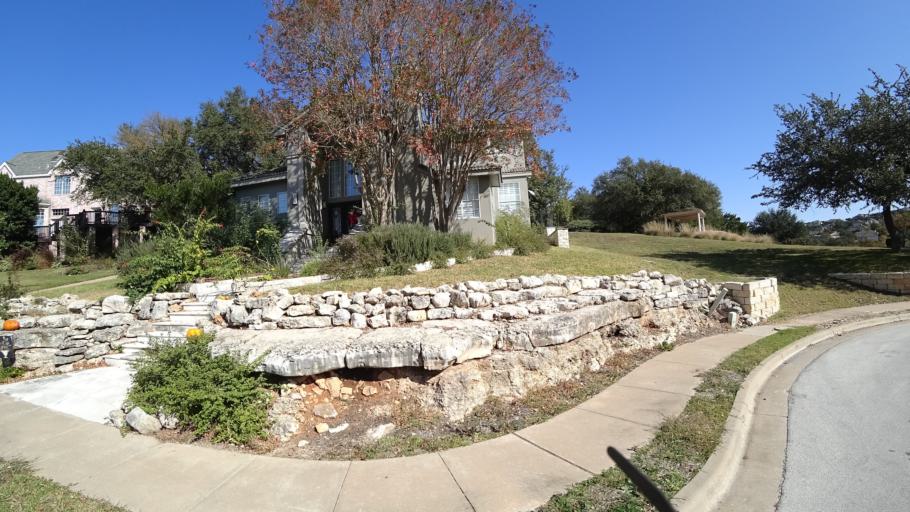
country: US
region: Texas
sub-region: Travis County
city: Lost Creek
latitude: 30.3661
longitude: -97.8630
